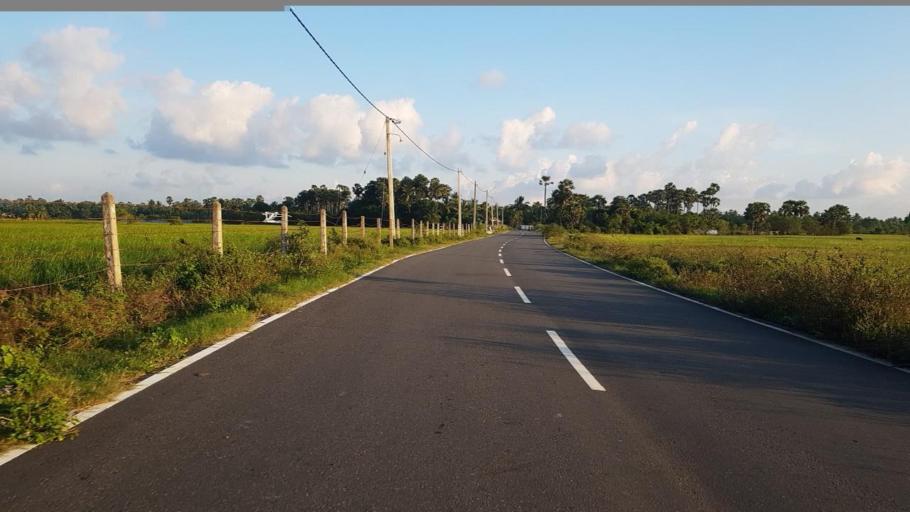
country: LK
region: Northern Province
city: Jaffna
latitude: 9.7250
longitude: 79.9761
